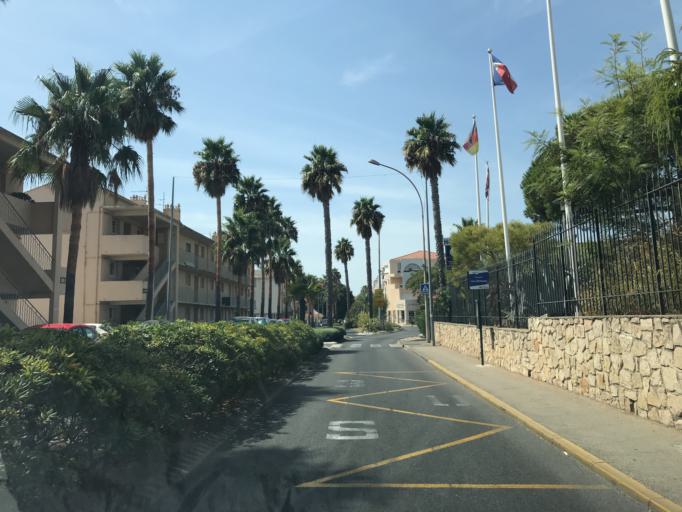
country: FR
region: Provence-Alpes-Cote d'Azur
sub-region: Departement du Var
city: Sanary-sur-Mer
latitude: 43.1186
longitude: 5.8098
